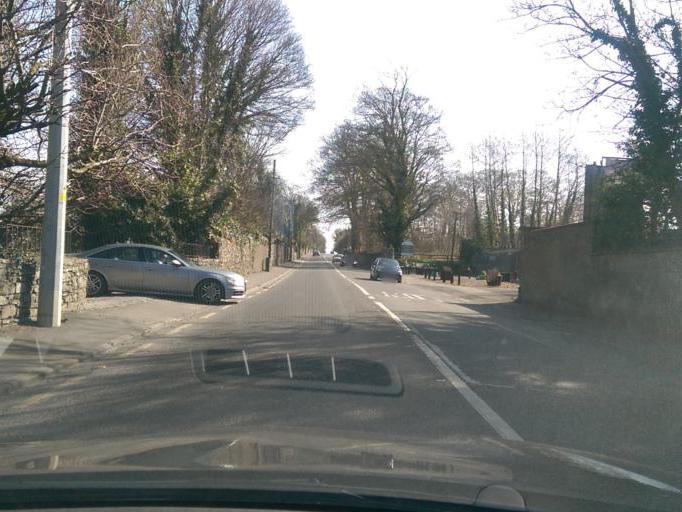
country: IE
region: Leinster
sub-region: Kildare
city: Leixlip
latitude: 53.3622
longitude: -6.4850
